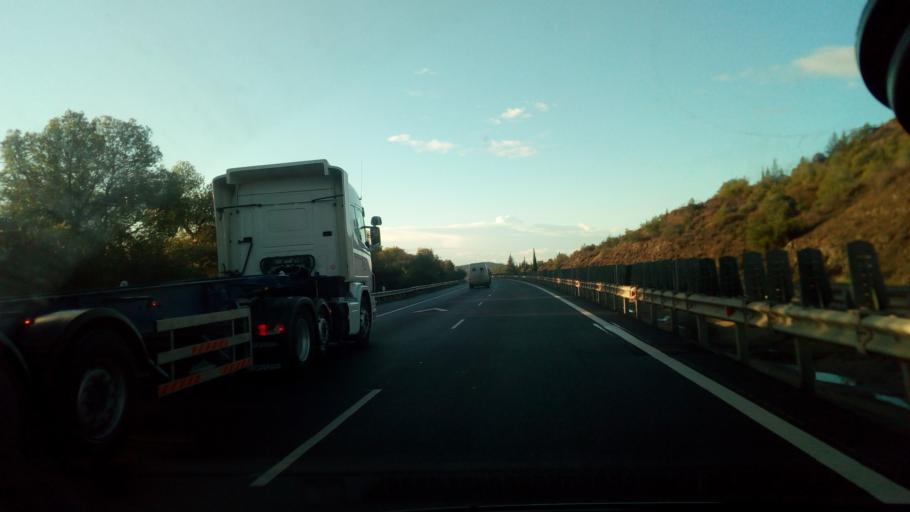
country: CY
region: Larnaka
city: Kornos
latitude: 34.8827
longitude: 33.3967
